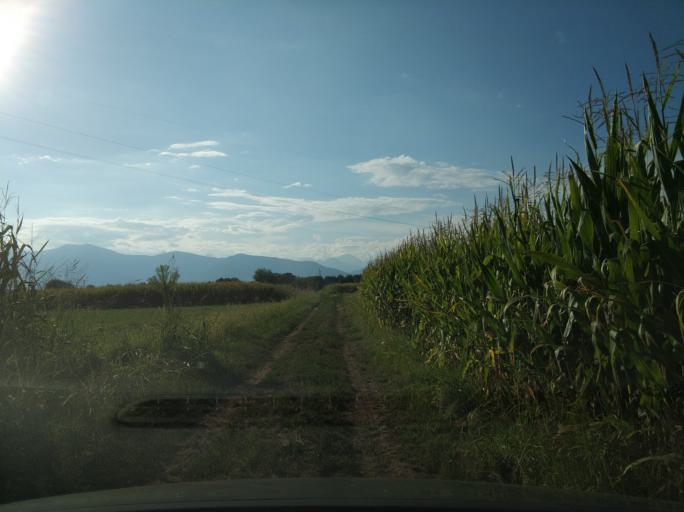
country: IT
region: Piedmont
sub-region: Provincia di Torino
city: Cirie
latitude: 45.2072
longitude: 7.6069
